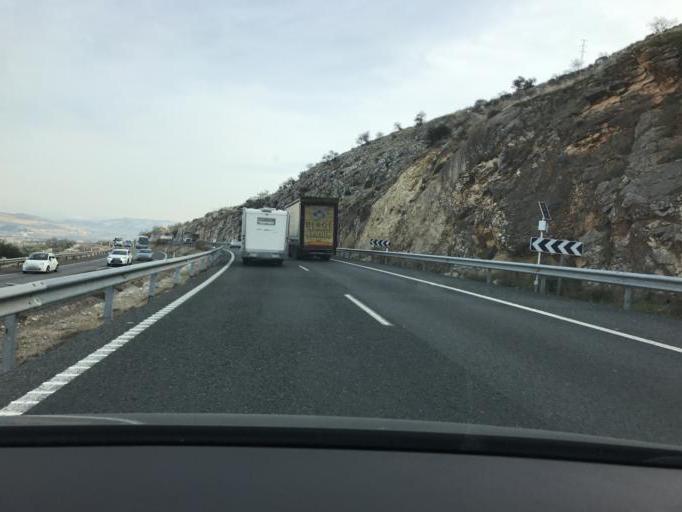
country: ES
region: Andalusia
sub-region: Provincia de Granada
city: Loja
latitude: 37.1593
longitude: -4.1463
